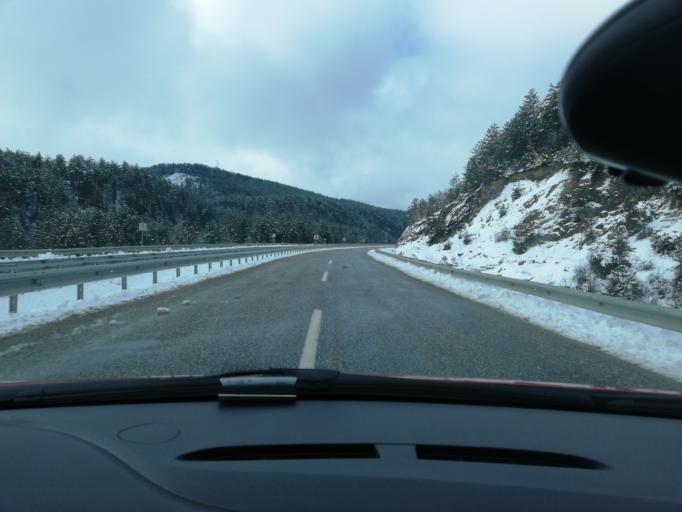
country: TR
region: Kastamonu
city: Akkaya
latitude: 41.2820
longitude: 33.4296
